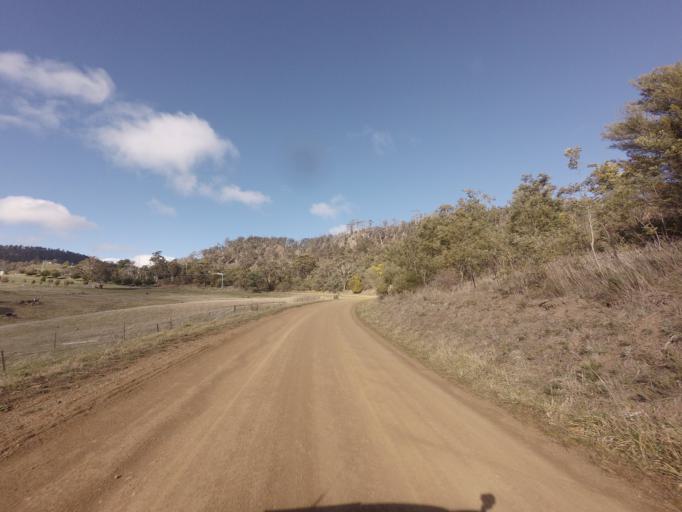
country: AU
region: Tasmania
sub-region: Derwent Valley
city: New Norfolk
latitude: -42.7041
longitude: 147.0041
